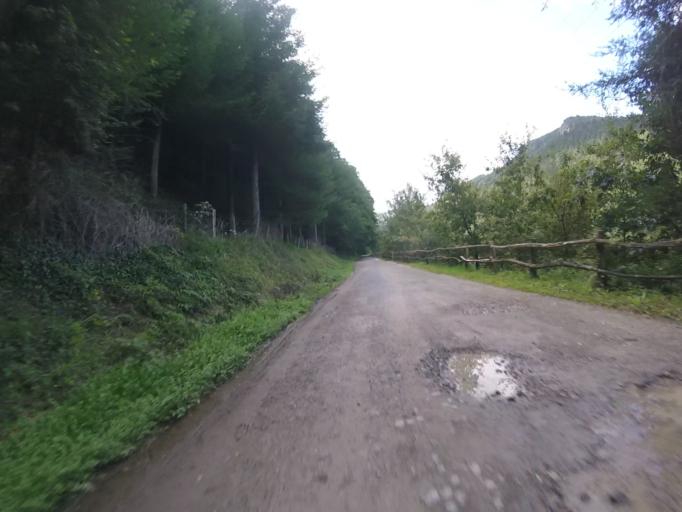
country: ES
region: Basque Country
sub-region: Provincia de Guipuzcoa
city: Andoain
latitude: 43.1982
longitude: -2.0110
